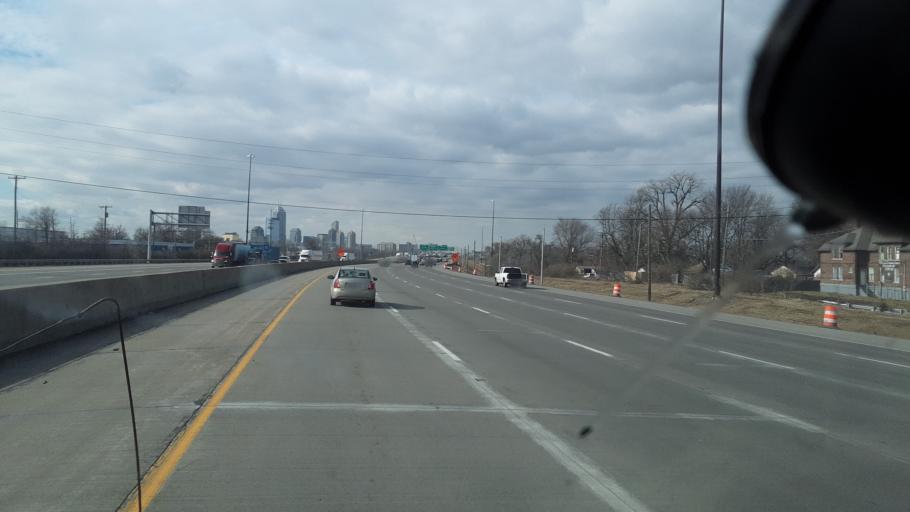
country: US
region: Indiana
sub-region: Marion County
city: Indianapolis
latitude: 39.7916
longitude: -86.1266
